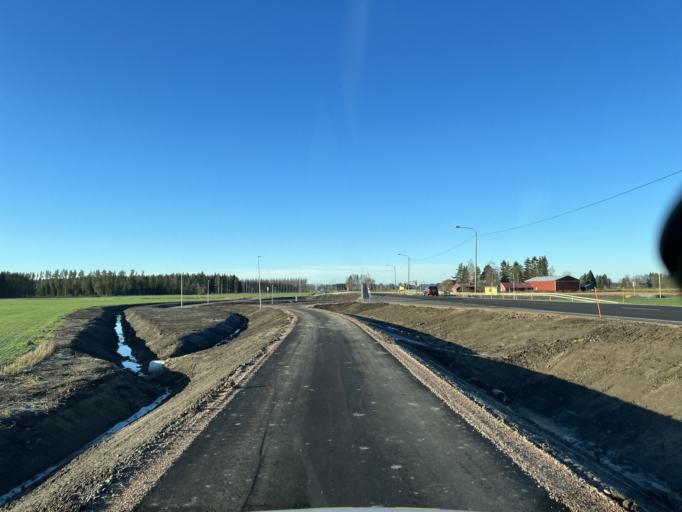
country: FI
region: Northern Ostrobothnia
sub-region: Nivala-Haapajaervi
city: Nivala
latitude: 63.9511
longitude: 24.9018
